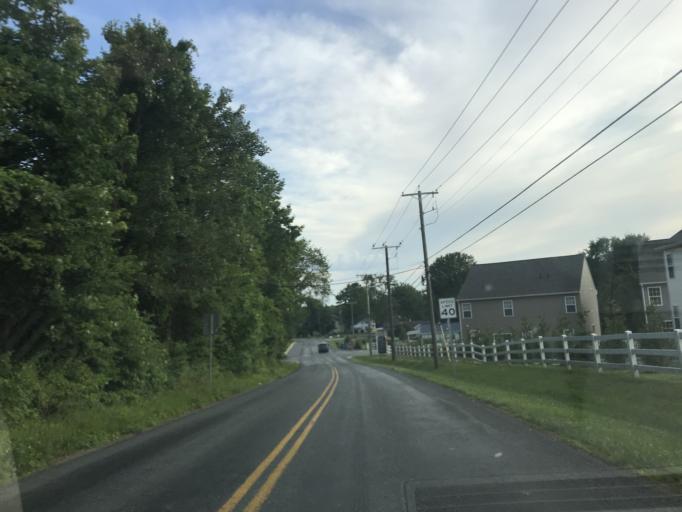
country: US
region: Maryland
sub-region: Harford County
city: Perryman
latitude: 39.5015
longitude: -76.2084
